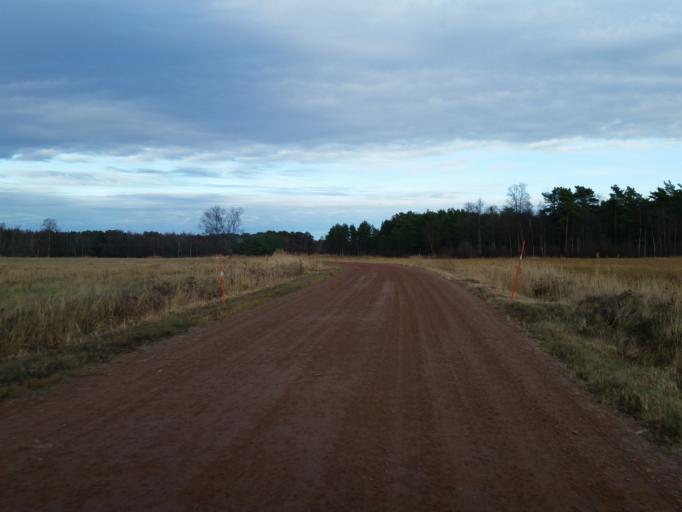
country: AX
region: Alands skaergard
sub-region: Kumlinge
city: Kumlinge
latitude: 60.2545
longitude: 20.8164
